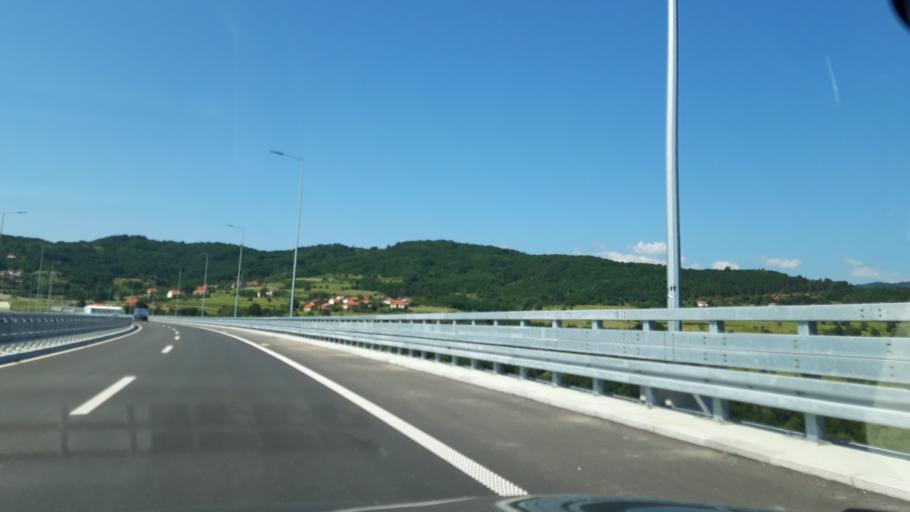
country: RS
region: Central Serbia
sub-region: Pcinjski Okrug
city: Vladicin Han
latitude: 42.7208
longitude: 22.0766
